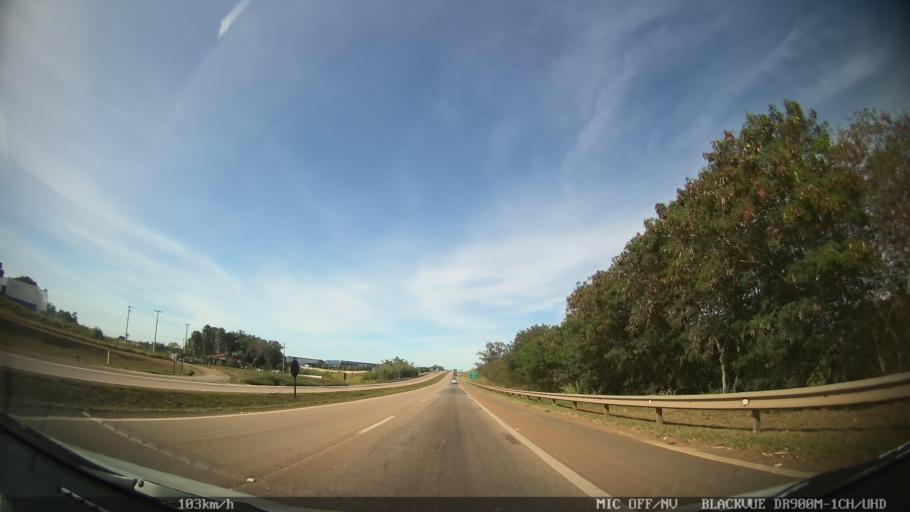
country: BR
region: Sao Paulo
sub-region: Rio Das Pedras
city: Rio das Pedras
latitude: -22.7867
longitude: -47.5850
